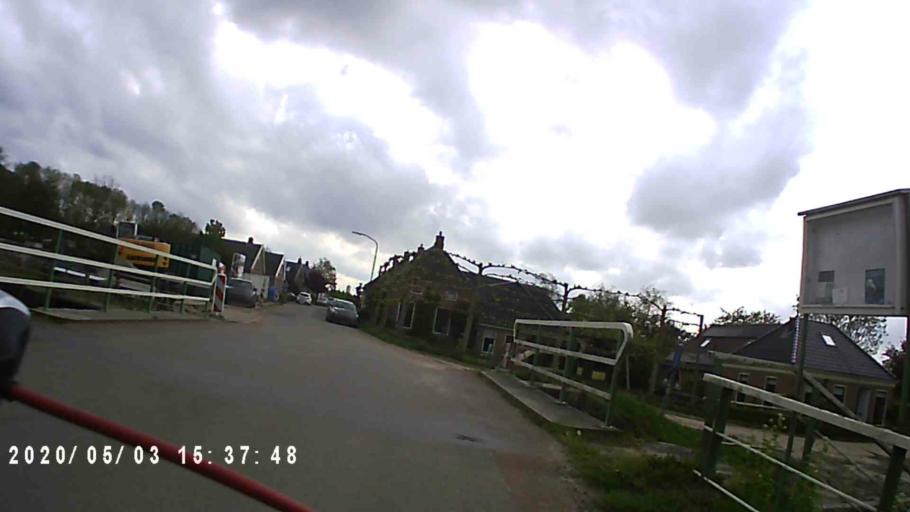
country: NL
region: Groningen
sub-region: Gemeente Zuidhorn
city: Oldehove
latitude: 53.3317
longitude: 6.4497
